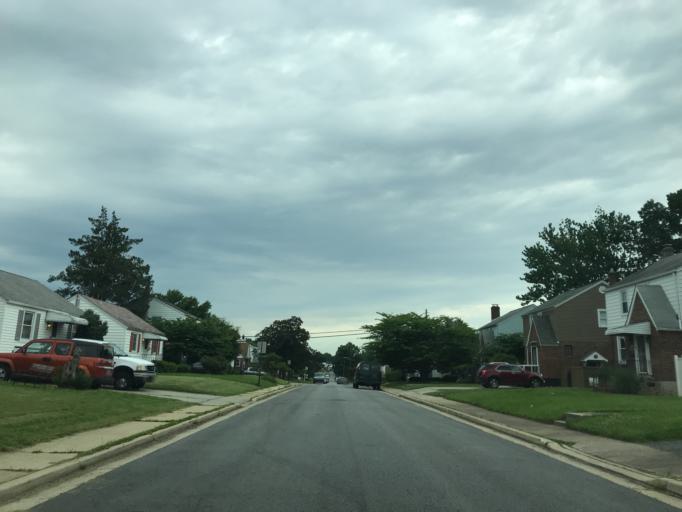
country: US
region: Maryland
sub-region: Baltimore County
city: Overlea
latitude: 39.3579
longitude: -76.5157
